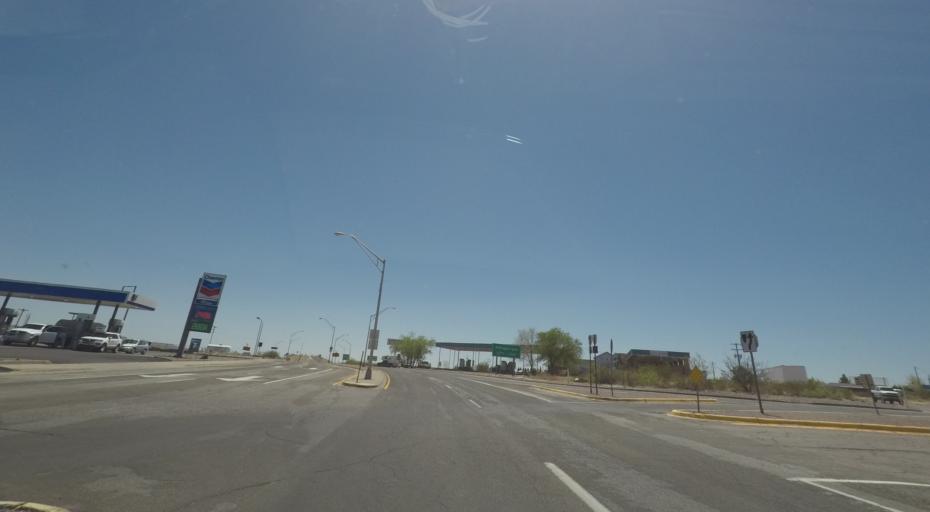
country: US
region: New Mexico
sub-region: Socorro County
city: Socorro
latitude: 34.0454
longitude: -106.8922
